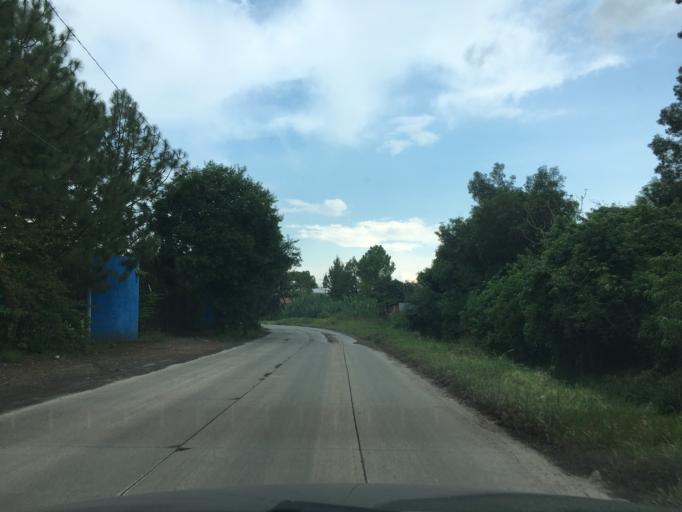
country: MX
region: Michoacan
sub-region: Morelia
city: Morelos
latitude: 19.6719
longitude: -101.2358
